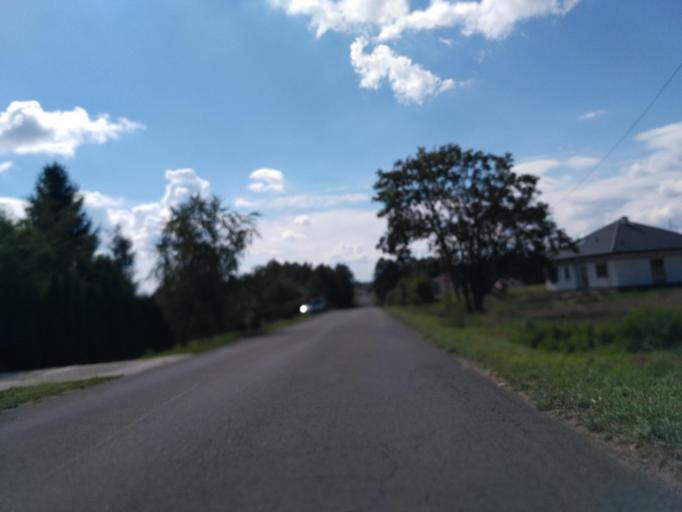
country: PL
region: Subcarpathian Voivodeship
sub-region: Powiat jasielski
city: Brzyska
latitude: 49.7938
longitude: 21.3982
